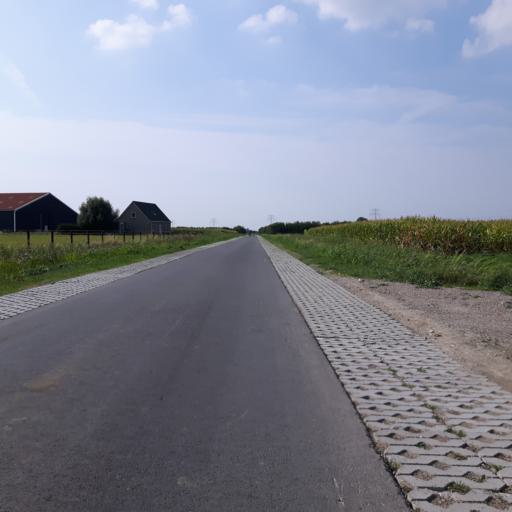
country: NL
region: Zeeland
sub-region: Gemeente Goes
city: Goes
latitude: 51.4657
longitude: 3.9378
